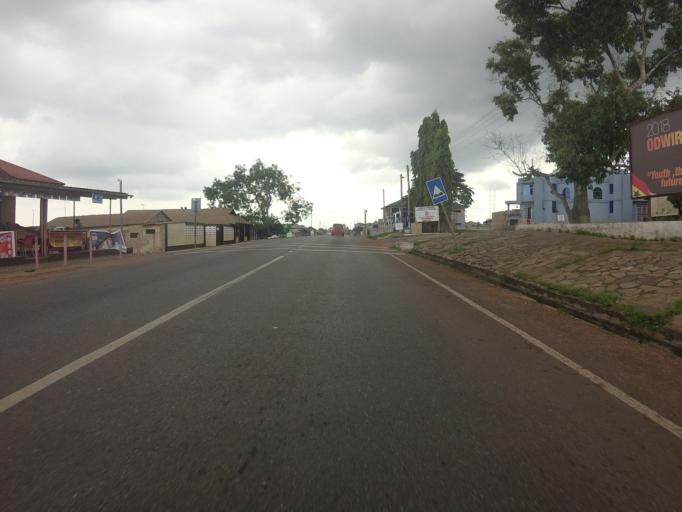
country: GH
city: Akropong
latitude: 5.9341
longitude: -0.1228
